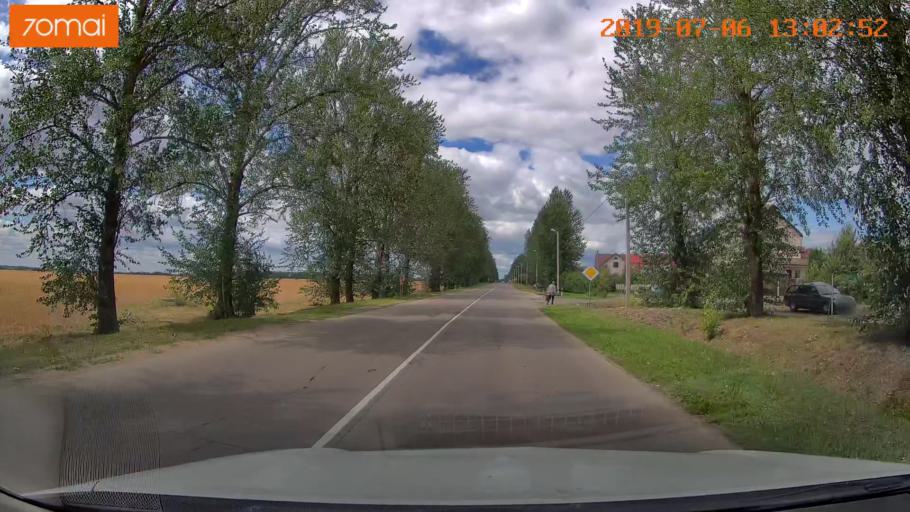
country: BY
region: Minsk
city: Dzyarzhynsk
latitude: 53.6874
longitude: 27.1102
